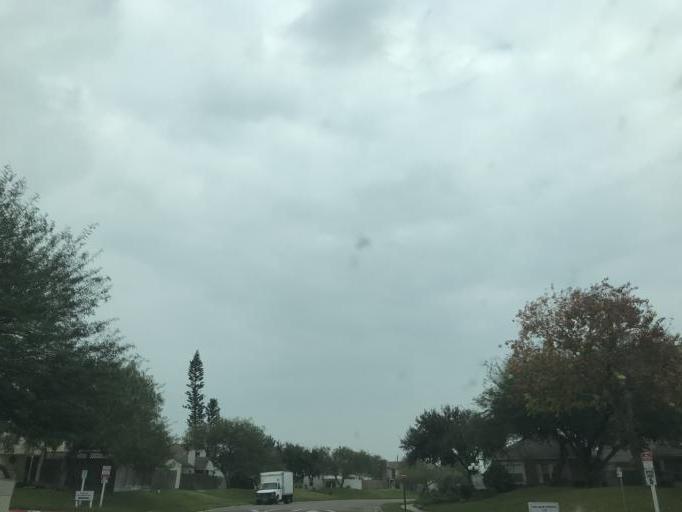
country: US
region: Texas
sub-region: Nueces County
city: Corpus Christi
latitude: 27.6689
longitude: -97.3542
